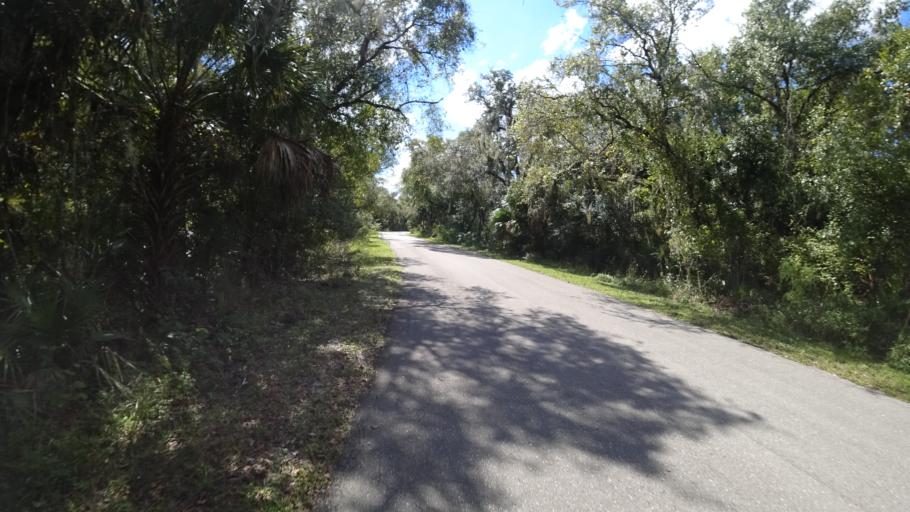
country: US
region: Florida
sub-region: Sarasota County
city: Lake Sarasota
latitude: 27.2836
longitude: -82.2584
